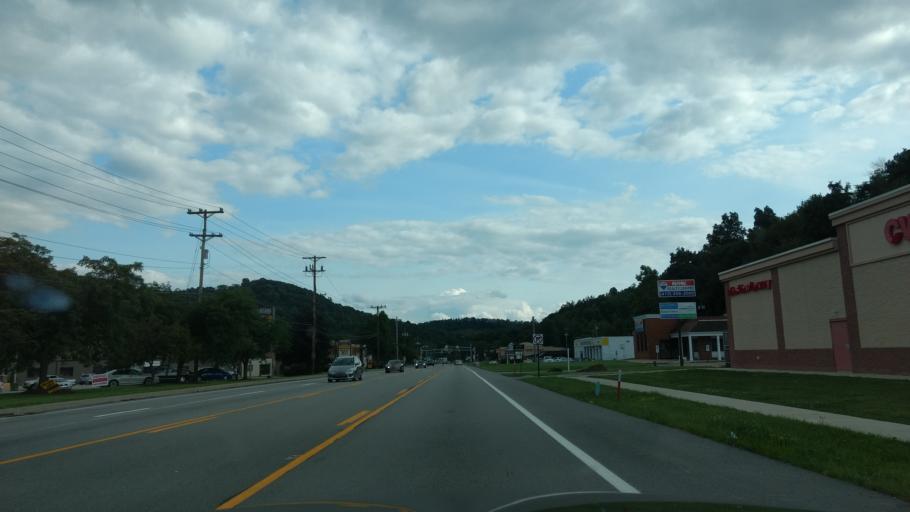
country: US
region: Pennsylvania
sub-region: Westmoreland County
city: Murrysville
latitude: 40.4449
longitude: -79.7137
